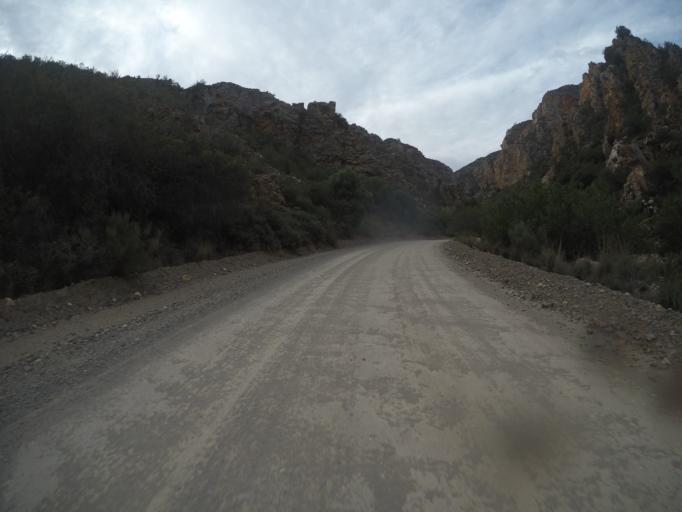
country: ZA
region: Eastern Cape
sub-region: Cacadu District Municipality
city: Willowmore
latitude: -33.5121
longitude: 23.6398
